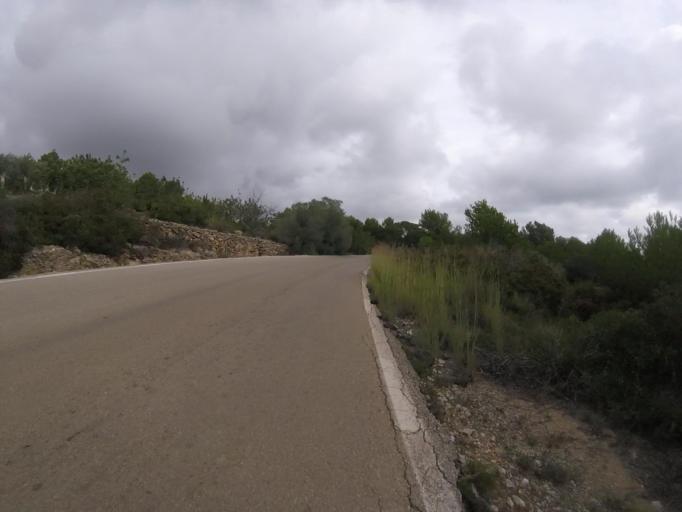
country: ES
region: Valencia
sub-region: Provincia de Castello
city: Cabanes
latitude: 40.1573
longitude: 0.0833
